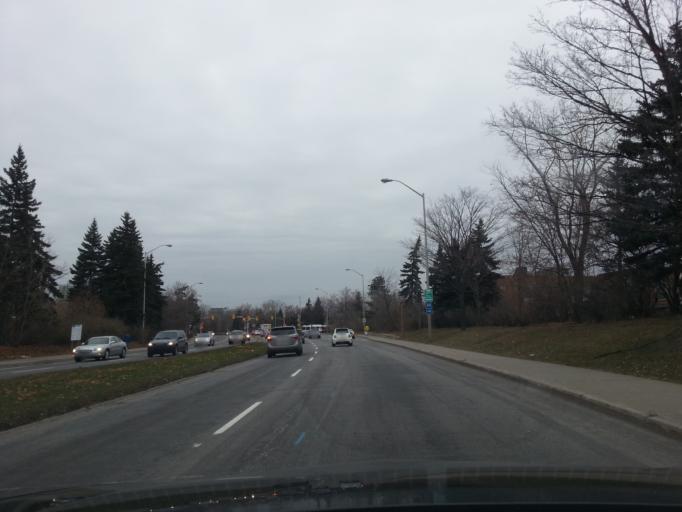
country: CA
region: Ontario
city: Ottawa
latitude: 45.4330
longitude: -75.6645
